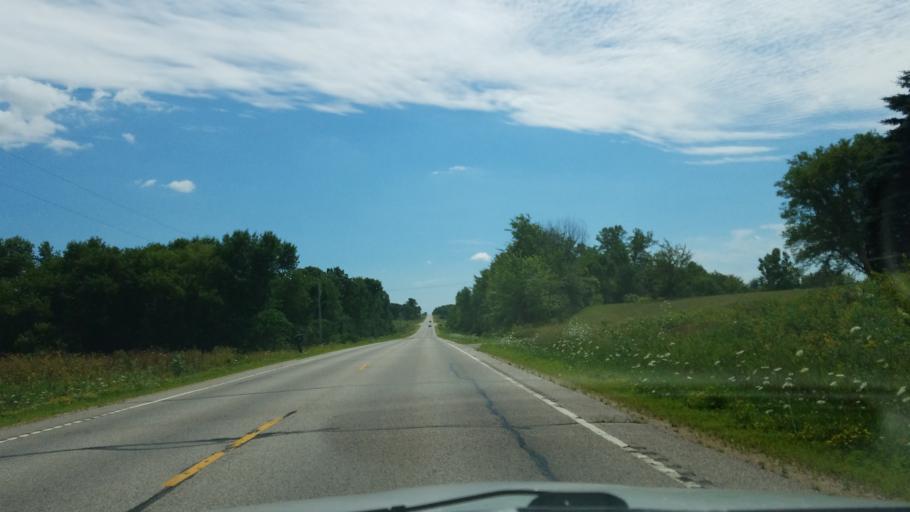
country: US
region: Wisconsin
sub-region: Saint Croix County
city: Glenwood City
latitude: 44.9934
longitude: -92.1966
